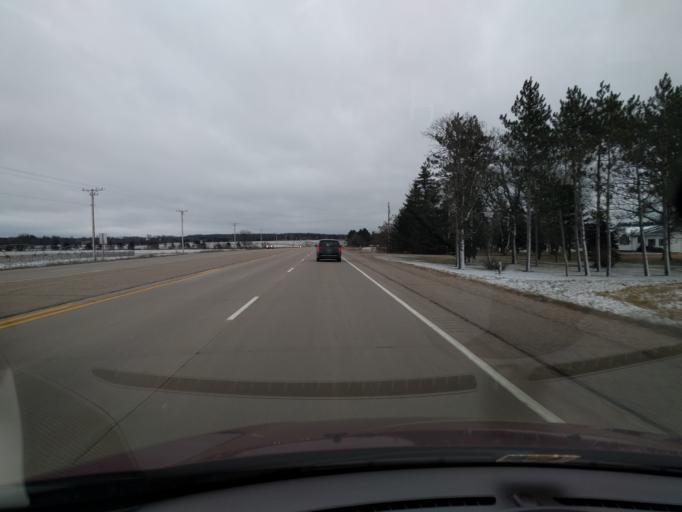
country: US
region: Wisconsin
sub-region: Portage County
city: Whiting
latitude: 44.5218
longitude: -89.4614
